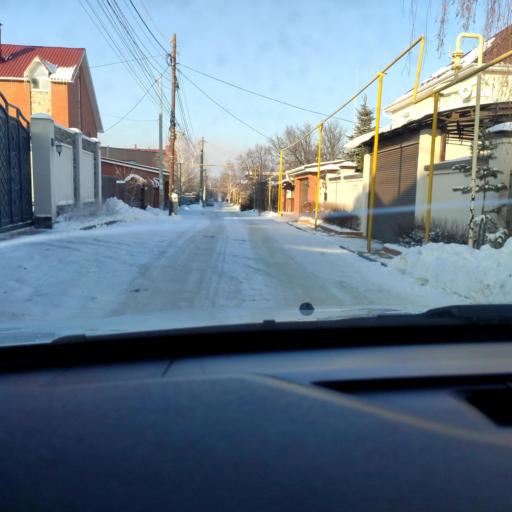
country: RU
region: Samara
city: Samara
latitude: 53.2709
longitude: 50.2048
